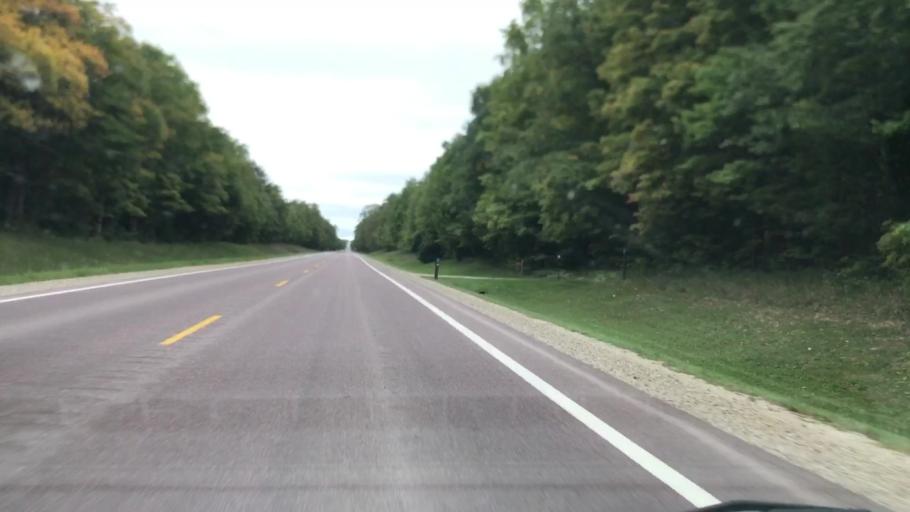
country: US
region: Michigan
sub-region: Luce County
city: Newberry
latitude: 46.2528
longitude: -85.5725
